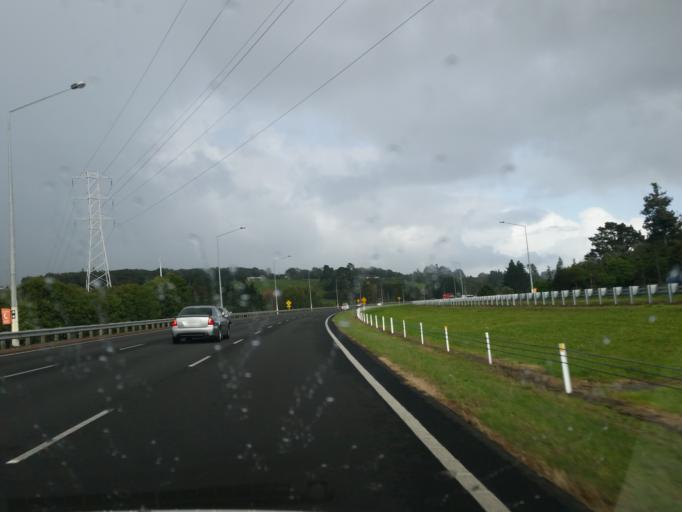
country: NZ
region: Auckland
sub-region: Auckland
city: Pukekohe East
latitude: -37.1684
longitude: 174.9847
